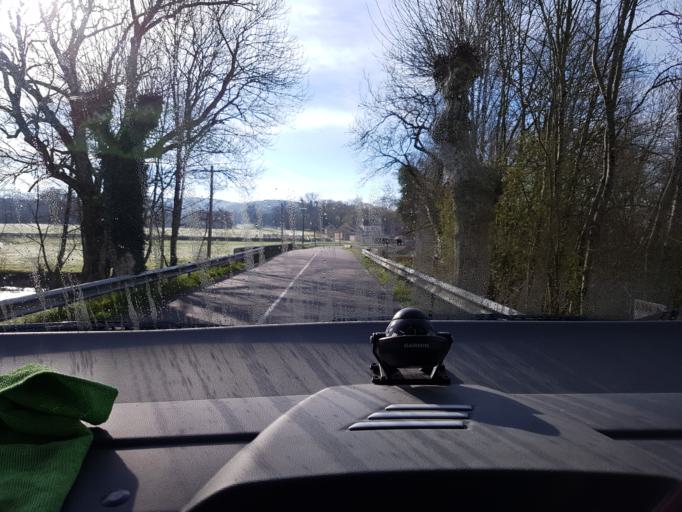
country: FR
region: Bourgogne
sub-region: Departement de Saone-et-Loire
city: Etang-sur-Arroux
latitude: 46.8609
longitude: 4.1928
